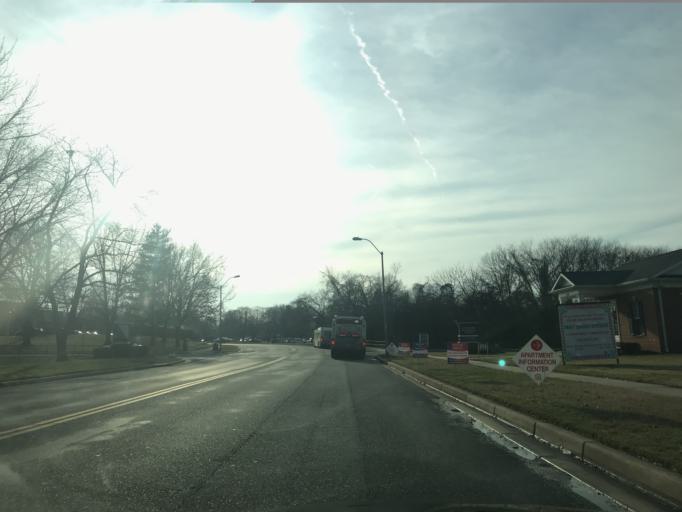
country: US
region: Maryland
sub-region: Baltimore County
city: Essex
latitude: 39.3013
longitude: -76.4453
